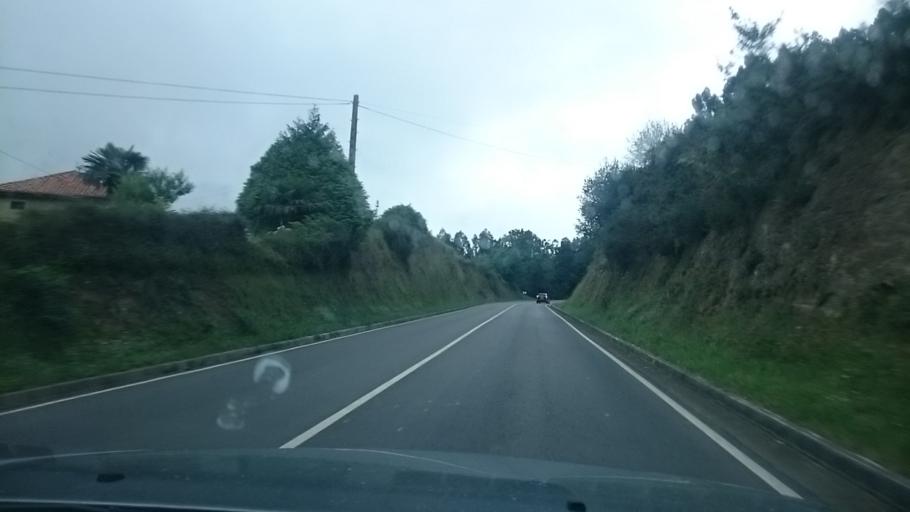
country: ES
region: Asturias
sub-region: Province of Asturias
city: Carrena
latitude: 43.4116
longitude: -4.8861
